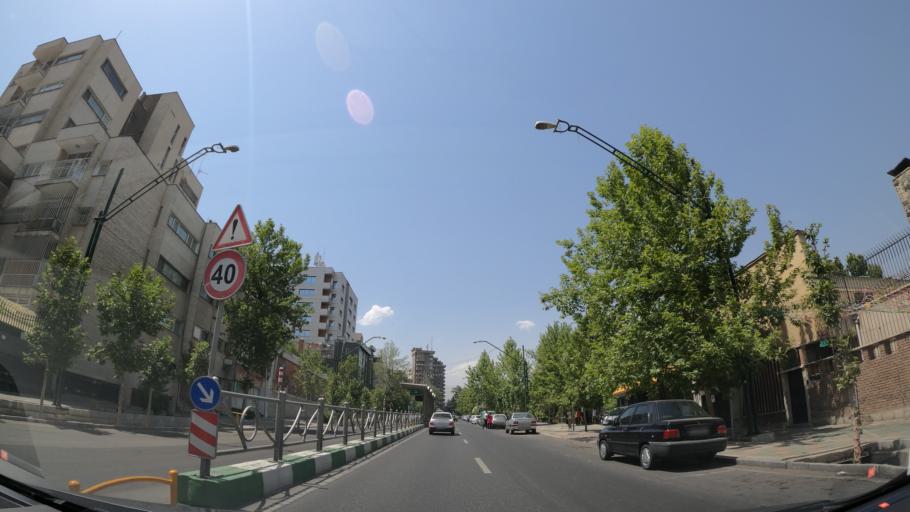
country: IR
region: Tehran
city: Tehran
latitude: 35.7347
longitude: 51.4101
